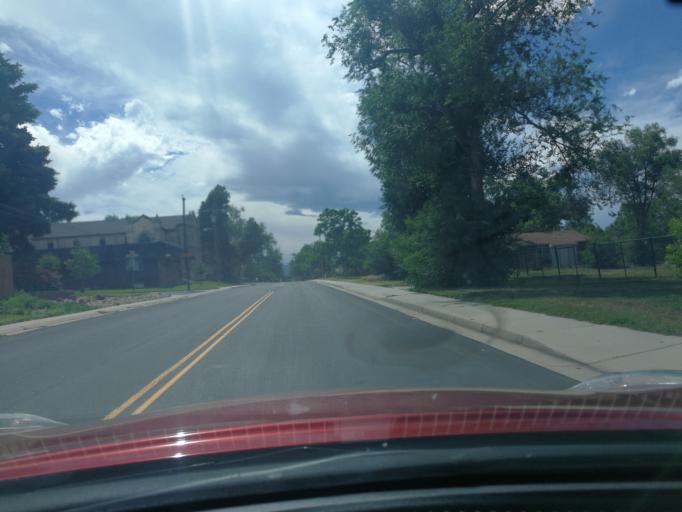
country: US
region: Colorado
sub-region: Arapahoe County
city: Littleton
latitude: 39.6151
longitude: -104.9978
